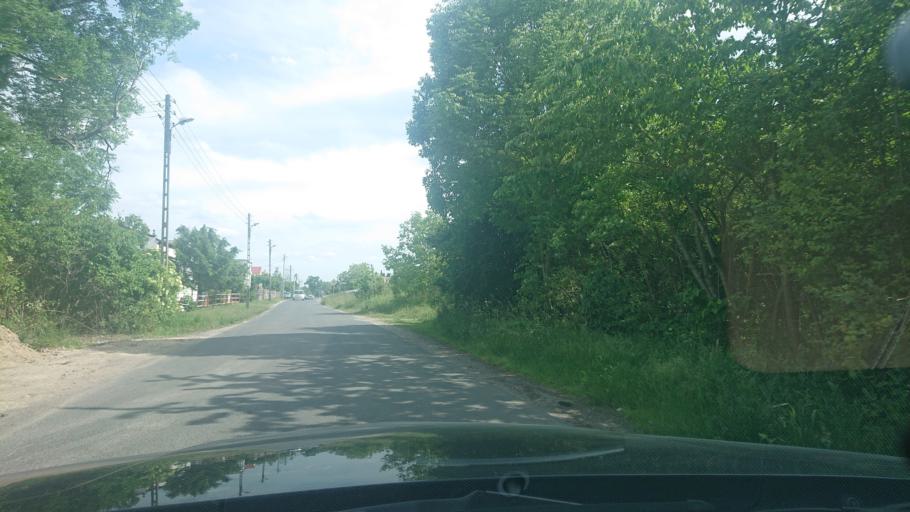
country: PL
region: Greater Poland Voivodeship
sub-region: Powiat gnieznienski
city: Gniezno
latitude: 52.5245
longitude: 17.6093
